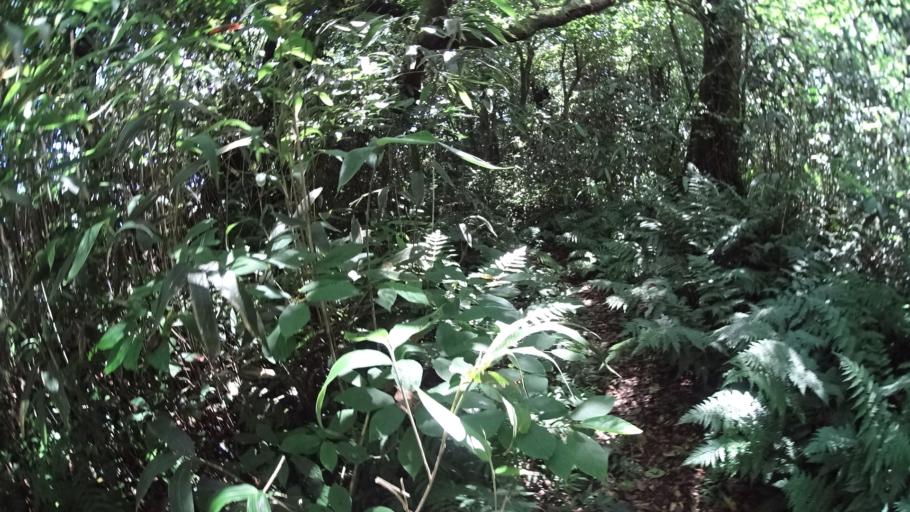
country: JP
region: Shizuoka
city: Shimoda
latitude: 34.5217
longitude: 139.2798
